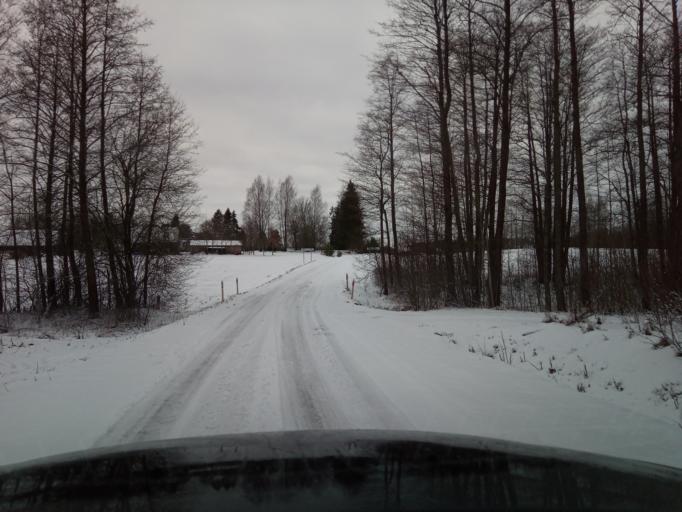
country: LT
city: Zarasai
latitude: 55.6750
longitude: 25.9828
